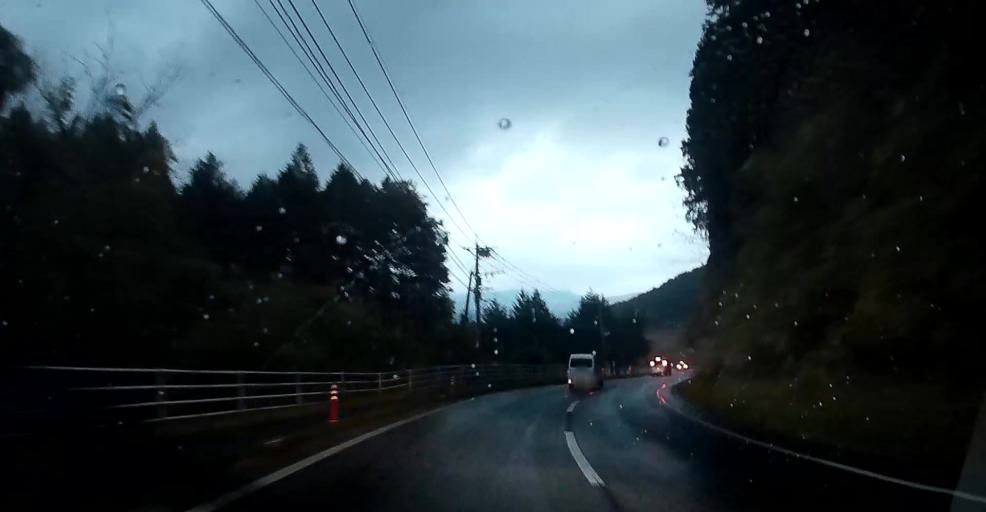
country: JP
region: Kumamoto
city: Ozu
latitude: 32.8370
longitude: 130.9155
